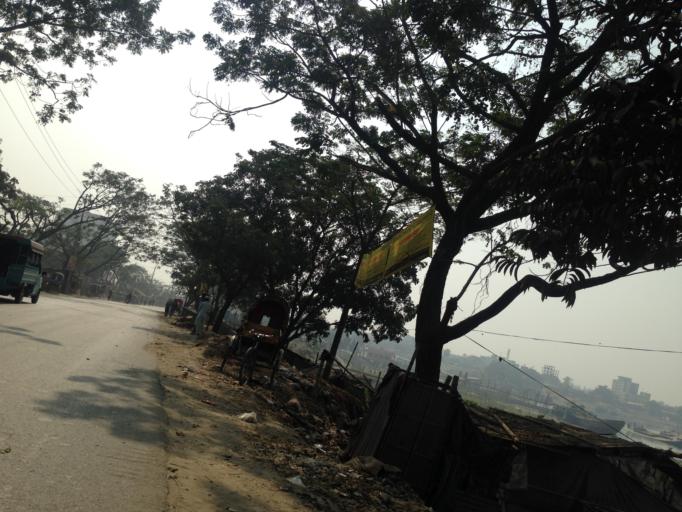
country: BD
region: Dhaka
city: Azimpur
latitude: 23.8022
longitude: 90.3439
